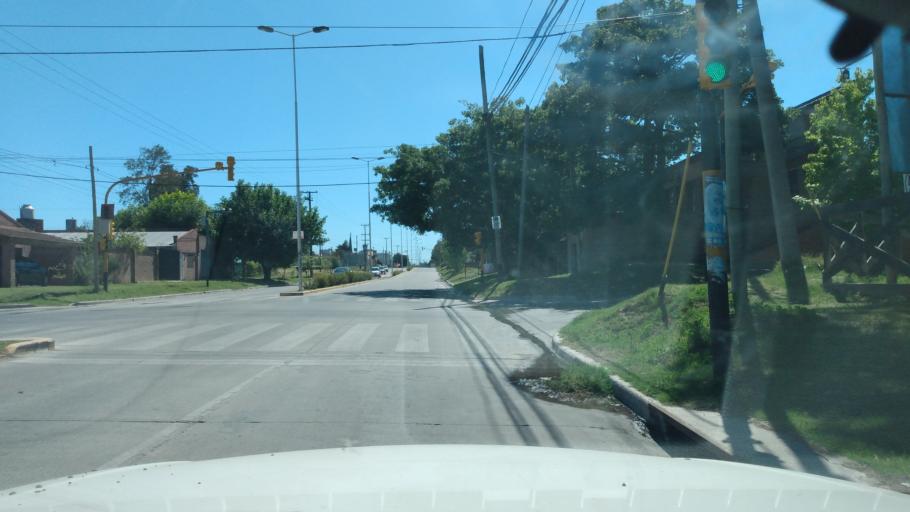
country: AR
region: Buenos Aires
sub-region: Partido de Lujan
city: Lujan
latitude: -34.5592
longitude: -59.1068
